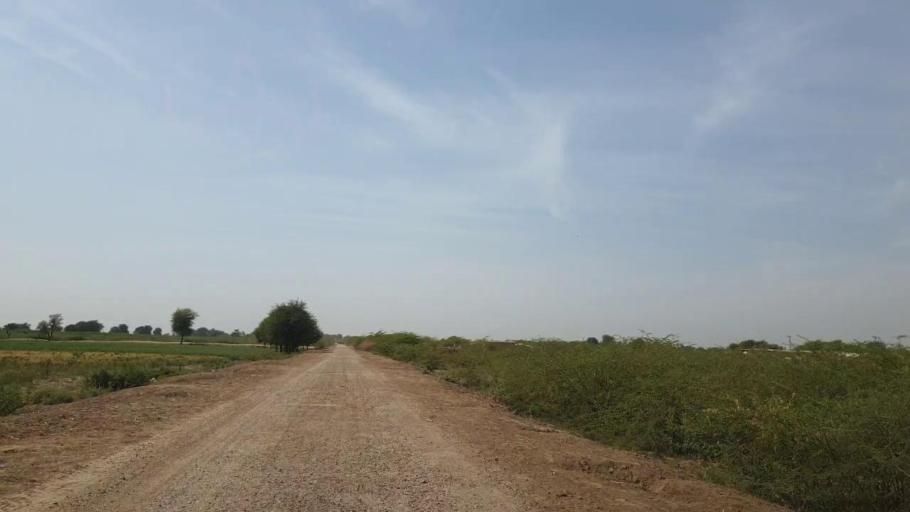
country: PK
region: Sindh
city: Kunri
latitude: 25.2051
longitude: 69.5498
